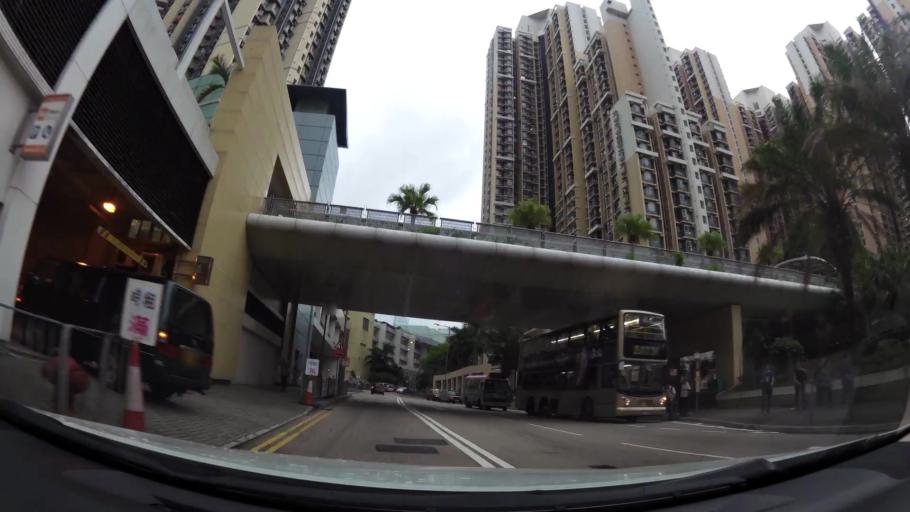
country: HK
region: Tsuen Wan
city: Tsuen Wan
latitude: 22.3681
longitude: 114.1276
